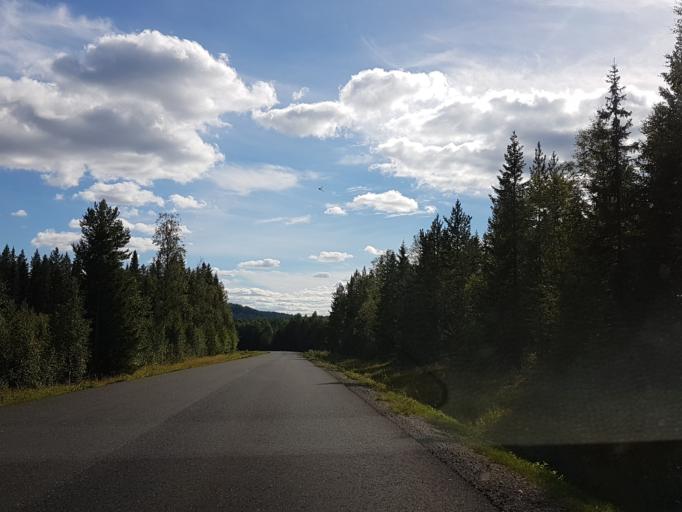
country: SE
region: Vaesterbotten
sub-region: Skelleftea Kommun
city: Burtraesk
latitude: 64.3075
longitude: 20.5296
